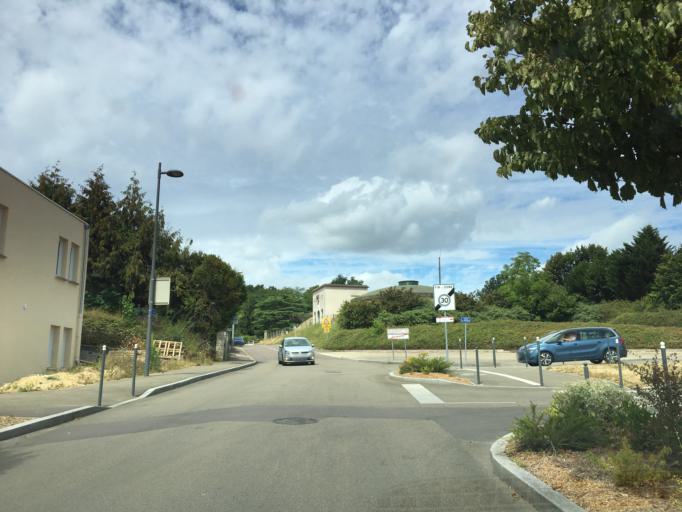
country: FR
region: Bourgogne
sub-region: Departement de l'Yonne
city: Saint-Georges-sur-Baulche
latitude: 47.8008
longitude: 3.5483
